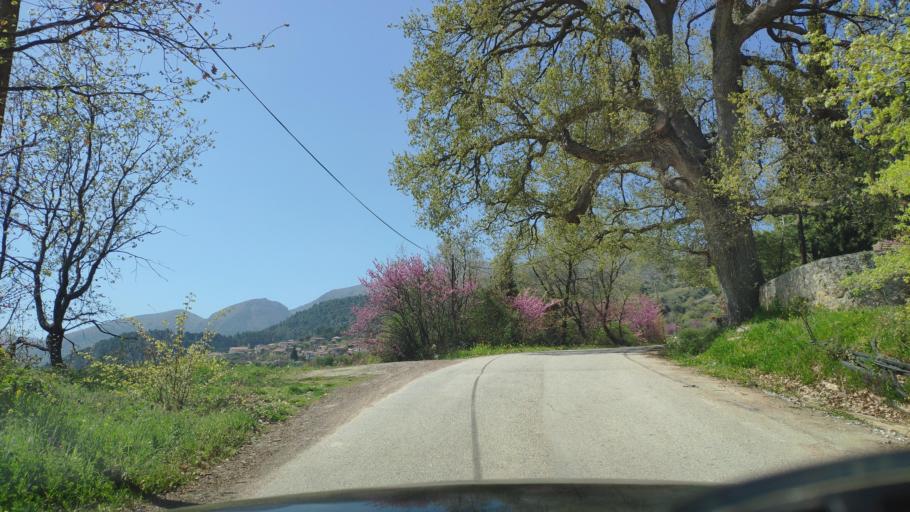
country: GR
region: West Greece
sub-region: Nomos Achaias
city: Akrata
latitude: 38.1082
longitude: 22.3174
